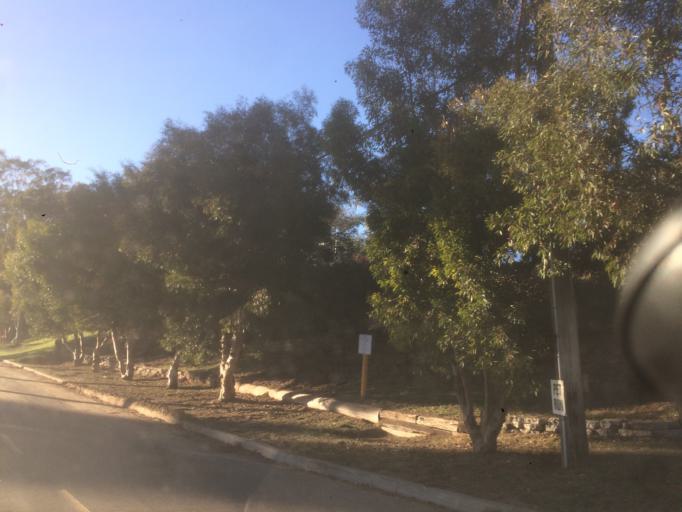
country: US
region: California
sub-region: Santa Barbara County
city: Mission Canyon
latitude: 34.4312
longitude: -119.7343
